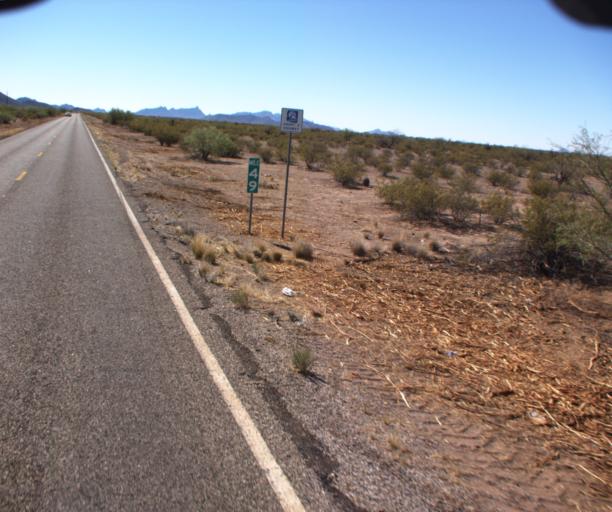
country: US
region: Arizona
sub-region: Pima County
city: Ajo
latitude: 32.3188
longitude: -112.7690
